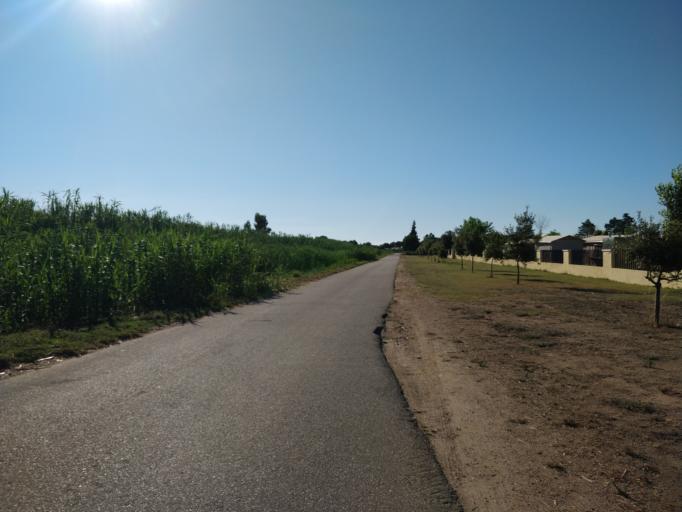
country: IT
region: Sardinia
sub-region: Provincia di Ogliastra
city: Lotzorai
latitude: 39.9609
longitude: 9.6779
